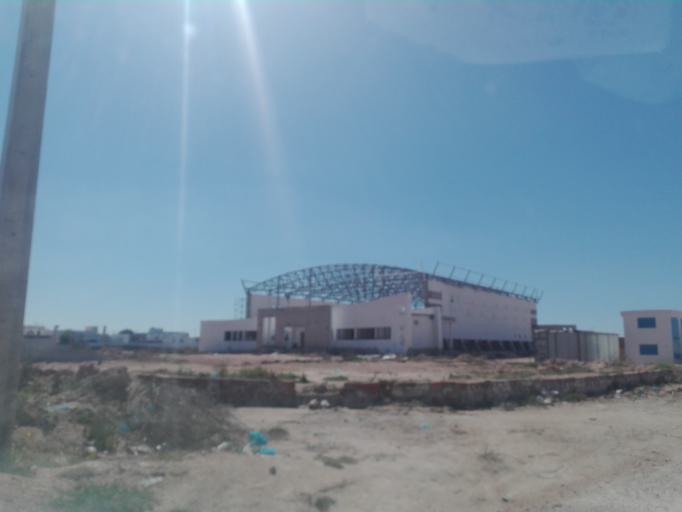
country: TN
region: Safaqis
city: Al Qarmadah
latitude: 34.7043
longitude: 11.1979
